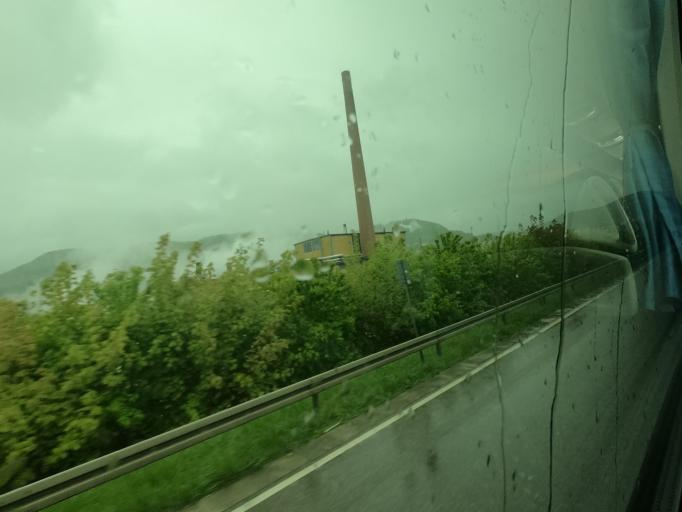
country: DE
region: Baden-Wuerttemberg
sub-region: Regierungsbezirk Stuttgart
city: Aalen
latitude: 48.8228
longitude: 10.1145
